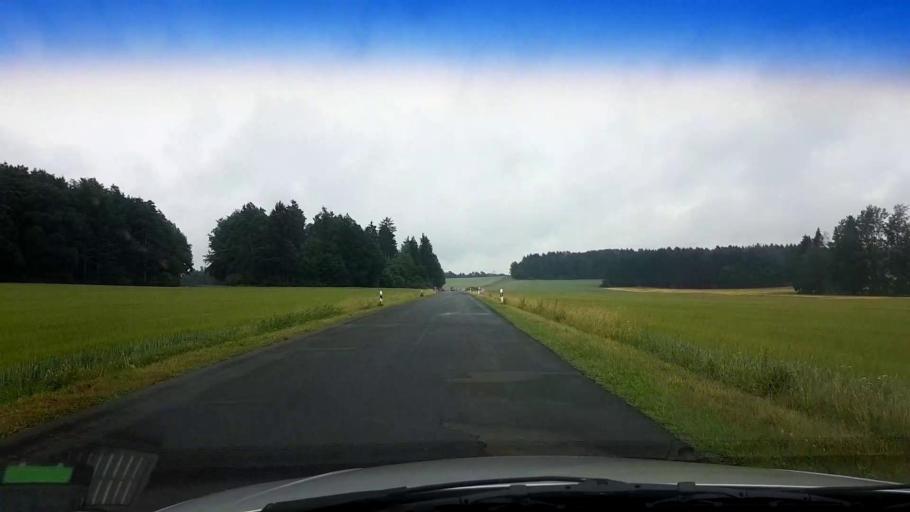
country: DE
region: Bavaria
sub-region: Upper Franconia
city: Wattendorf
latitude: 50.0568
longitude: 11.1166
